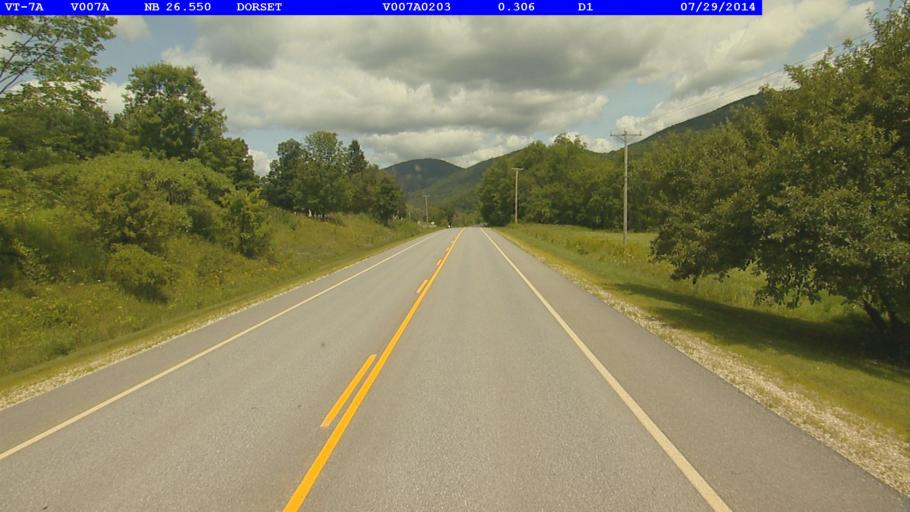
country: US
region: Vermont
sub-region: Bennington County
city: Manchester Center
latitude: 43.2147
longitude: -73.0163
